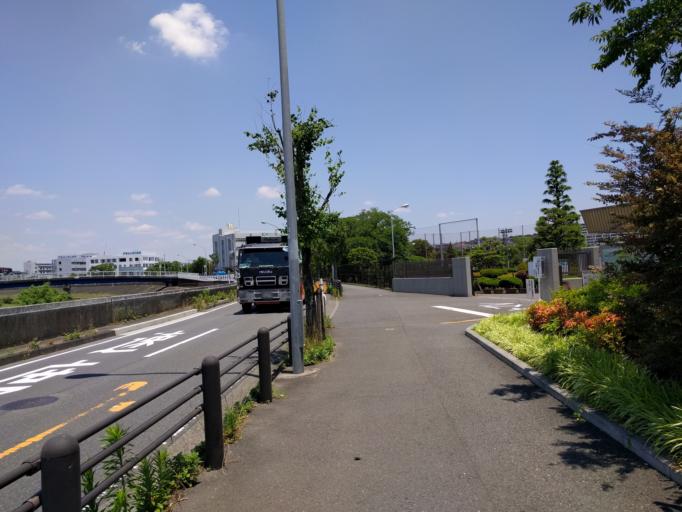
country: JP
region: Kanagawa
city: Fujisawa
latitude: 35.4023
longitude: 139.5375
